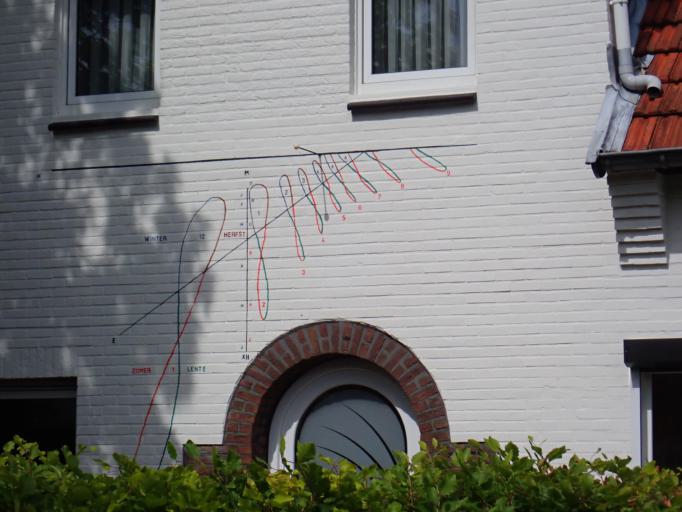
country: BE
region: Flanders
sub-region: Provincie Antwerpen
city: Kalmthout
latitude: 51.3691
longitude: 4.4609
